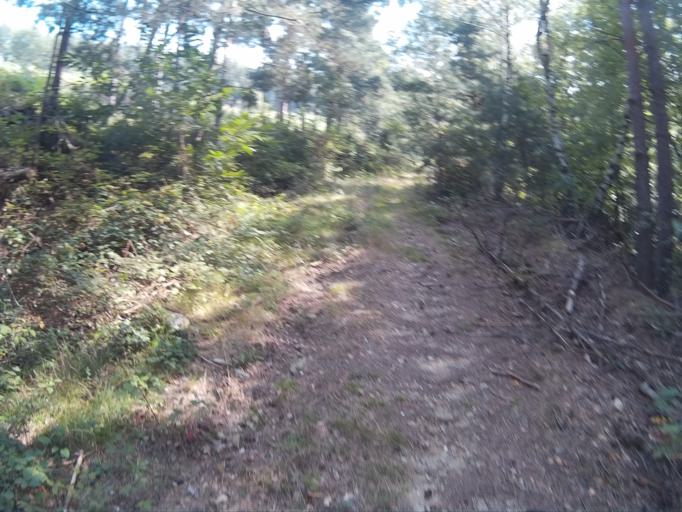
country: AT
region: Burgenland
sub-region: Politischer Bezirk Oberpullendorf
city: Mannersdorf an der Rabnitz
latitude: 47.4016
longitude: 16.5102
